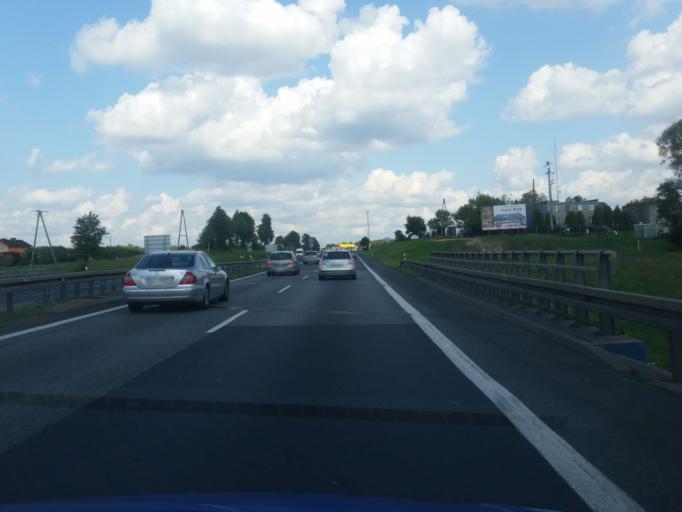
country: PL
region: Silesian Voivodeship
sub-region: Powiat myszkowski
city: Kozieglowy
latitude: 50.6003
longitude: 19.1505
